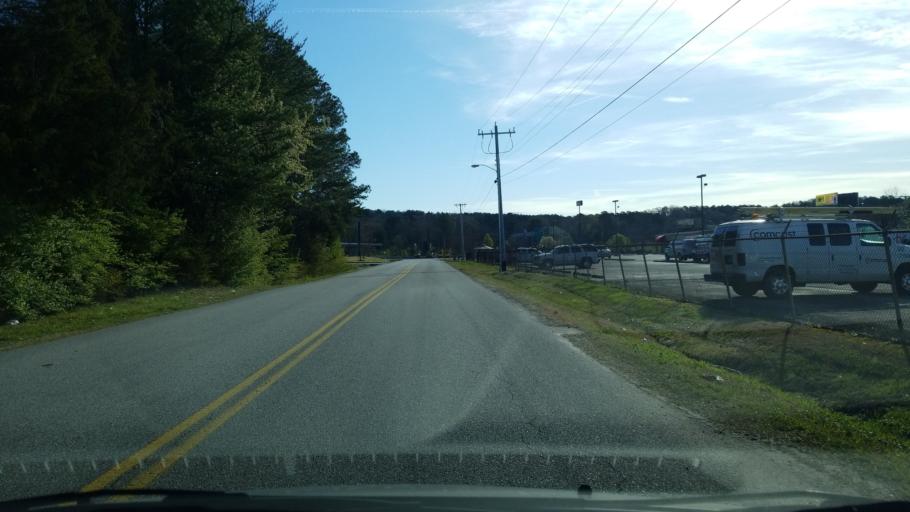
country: US
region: Tennessee
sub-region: Hamilton County
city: East Chattanooga
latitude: 35.0445
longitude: -85.1900
